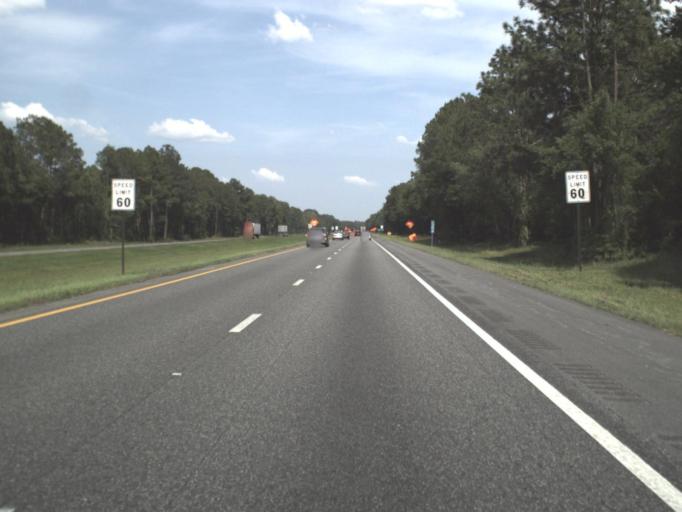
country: US
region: Florida
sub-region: Columbia County
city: Five Points
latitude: 30.2413
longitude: -82.6311
